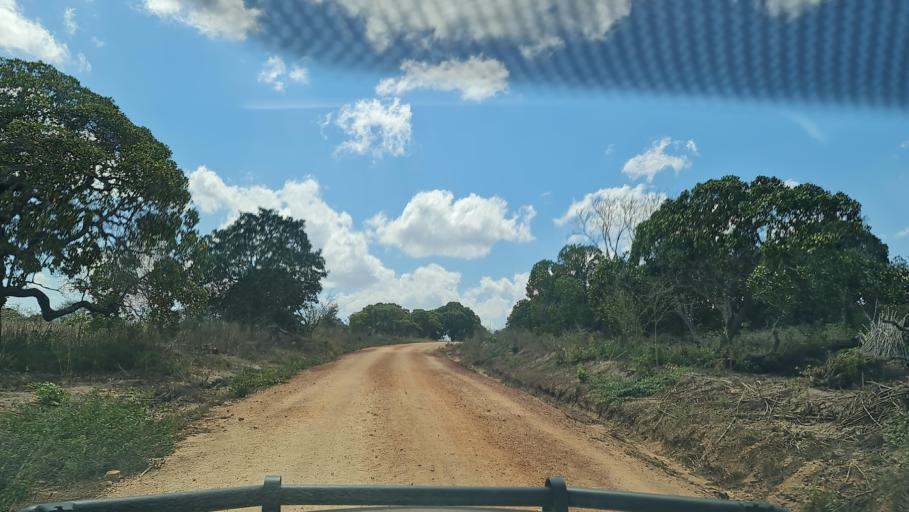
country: MZ
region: Nampula
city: Nacala
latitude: -14.1692
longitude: 40.2557
